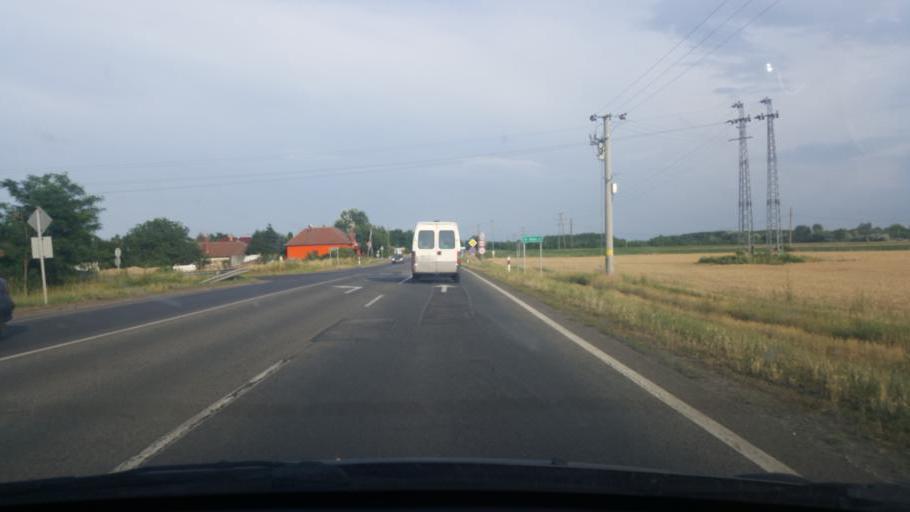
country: HU
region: Pest
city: Ullo
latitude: 47.3648
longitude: 19.3831
